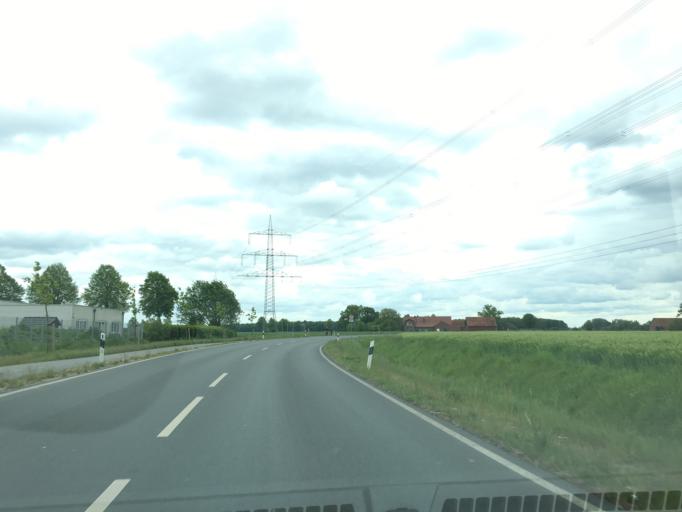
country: DE
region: North Rhine-Westphalia
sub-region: Regierungsbezirk Munster
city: Senden
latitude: 51.9425
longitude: 7.5272
